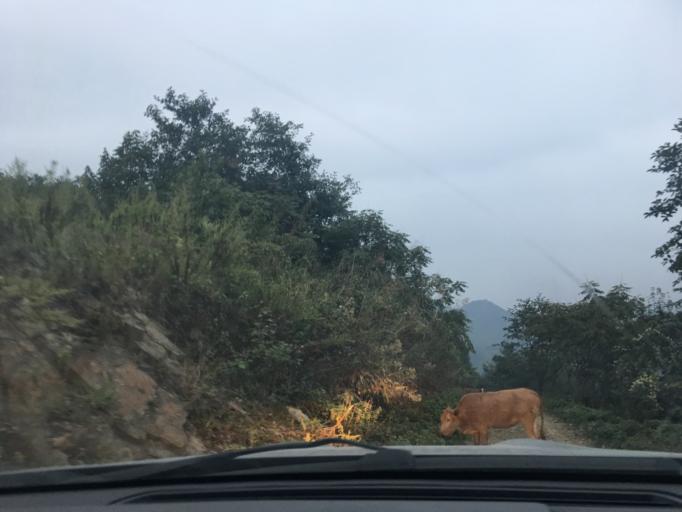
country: CN
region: Guangxi Zhuangzu Zizhiqu
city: Xinzhou
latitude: 24.9029
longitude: 105.5879
